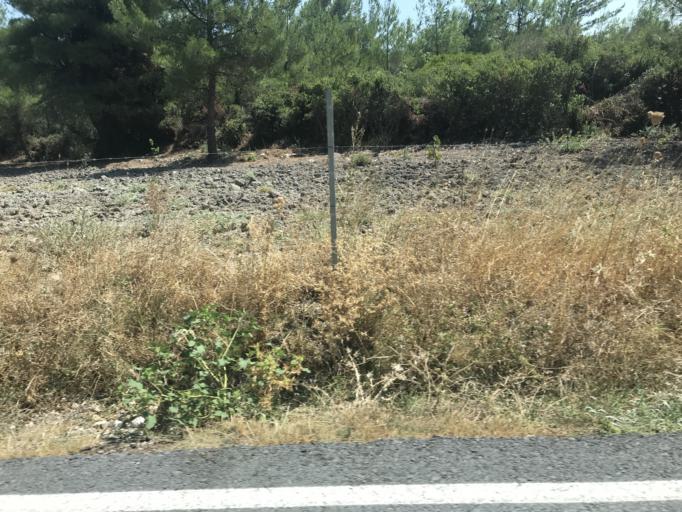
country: TR
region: Izmir
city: Urla
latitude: 38.2619
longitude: 26.7378
